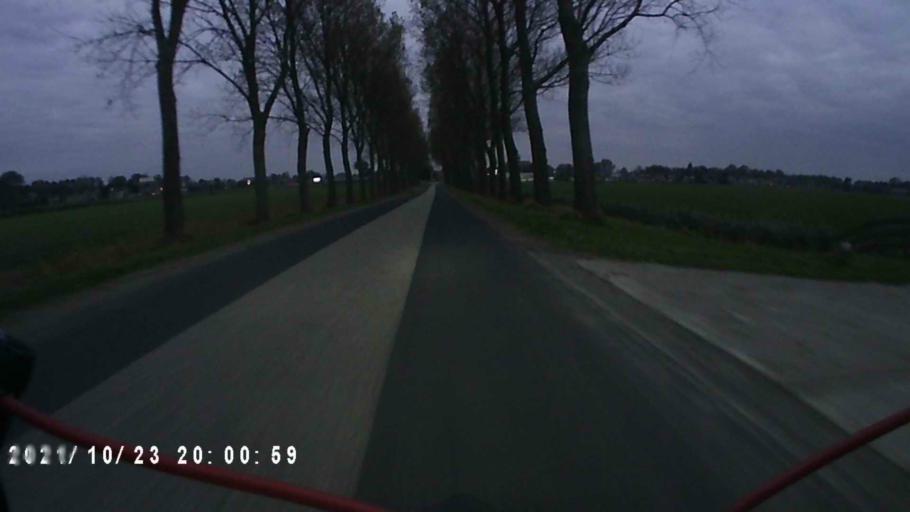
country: NL
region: Friesland
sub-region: Gemeente Harlingen
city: Harlingen
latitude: 53.1069
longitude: 5.4628
